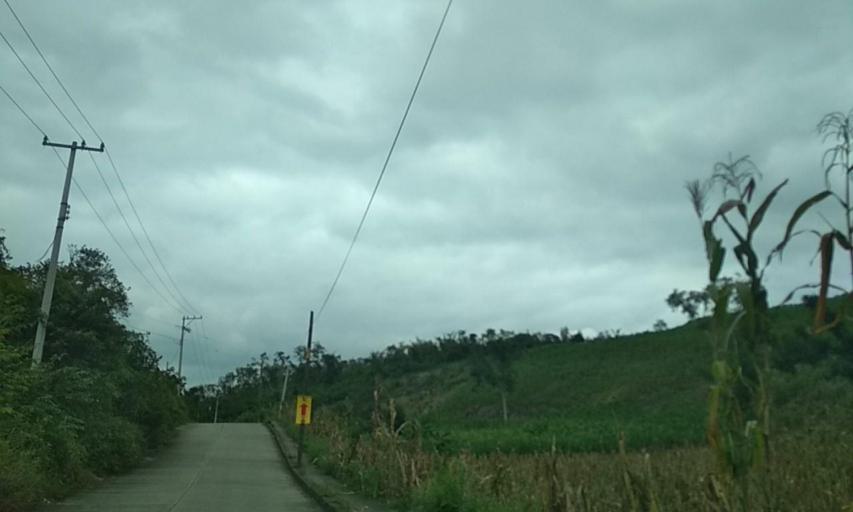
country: MX
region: Veracruz
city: Papantla de Olarte
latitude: 20.4709
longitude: -97.3202
